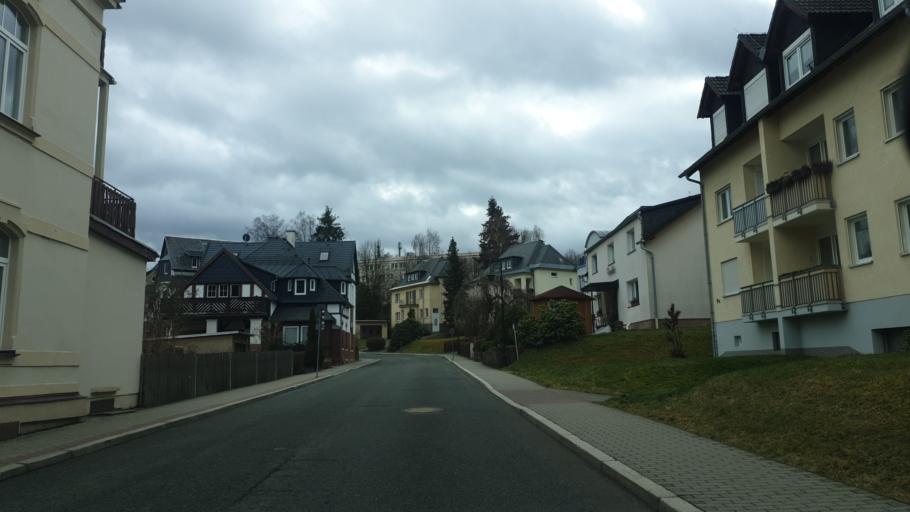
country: DE
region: Saxony
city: Bad Elster
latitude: 50.2834
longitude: 12.2308
